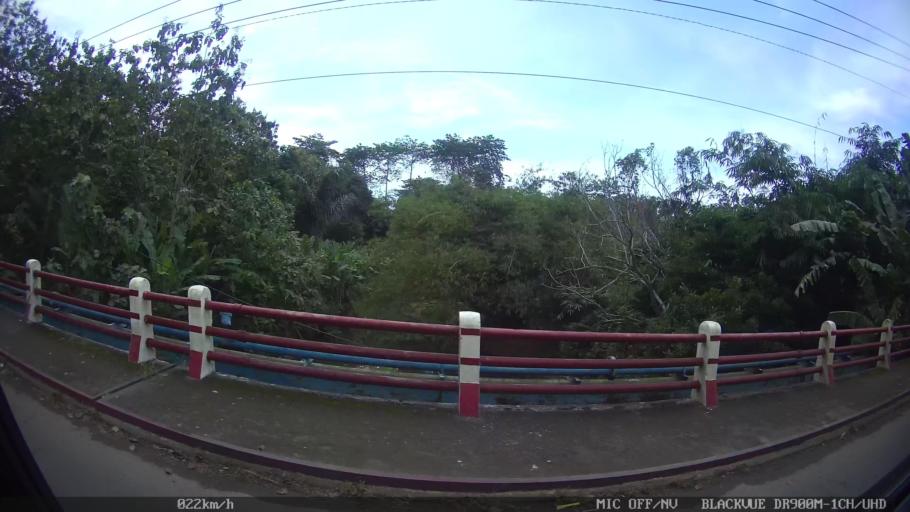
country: ID
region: Lampung
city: Bandarlampung
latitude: -5.4361
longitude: 105.2358
